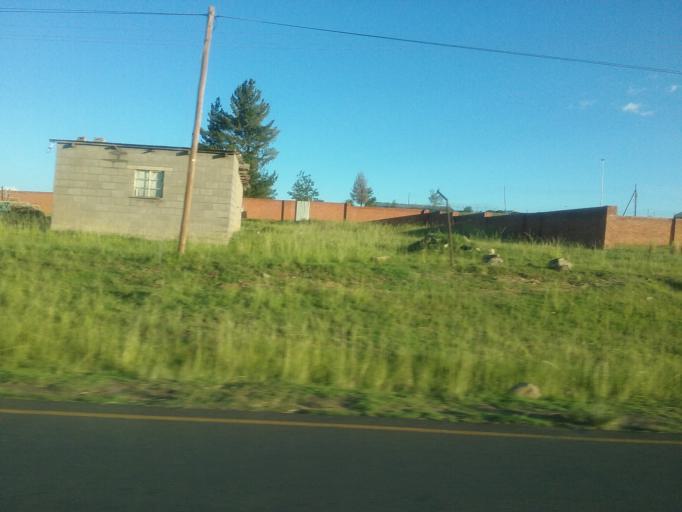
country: LS
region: Maseru
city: Maseru
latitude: -29.2659
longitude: 27.5421
